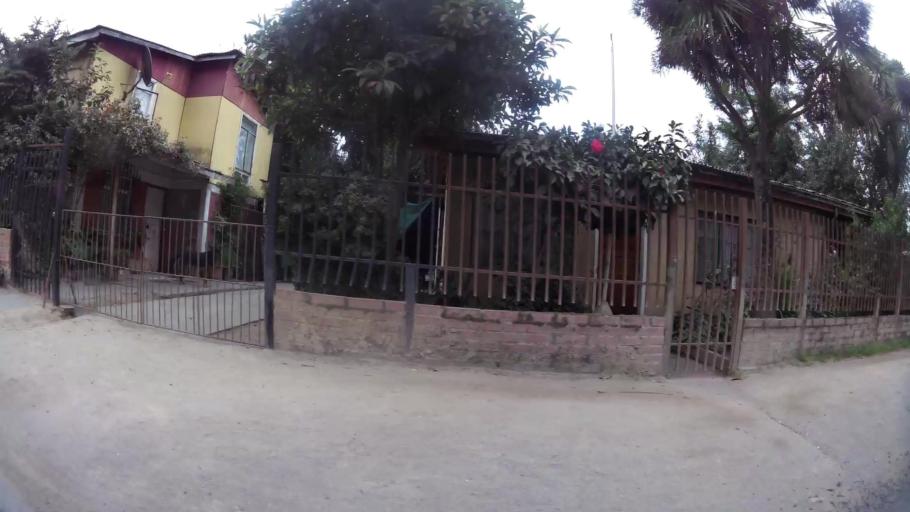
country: CL
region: Biobio
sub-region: Provincia de Concepcion
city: Concepcion
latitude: -36.8205
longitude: -72.9900
